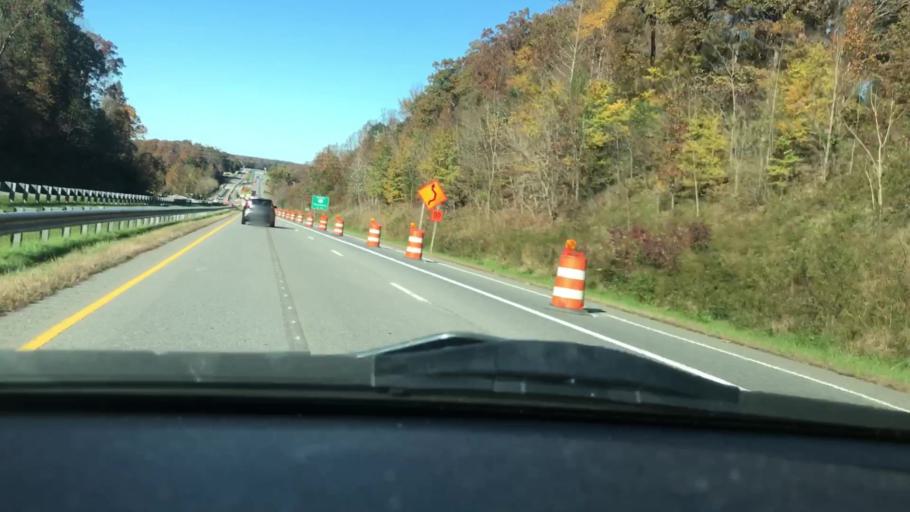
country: US
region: North Carolina
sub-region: Rockingham County
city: Stoneville
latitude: 36.4352
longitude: -79.9299
